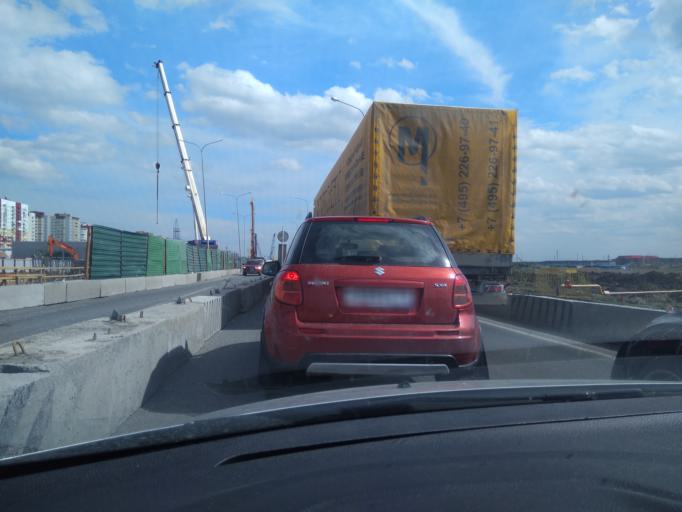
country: RU
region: Tjumen
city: Tyumen
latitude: 57.1065
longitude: 65.5574
